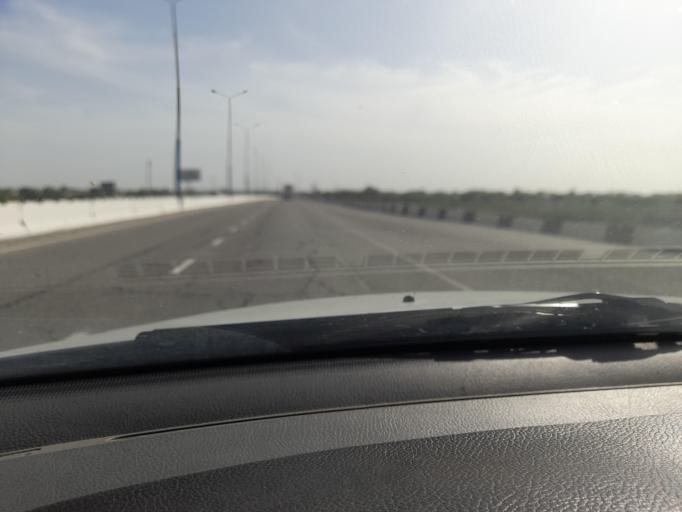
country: UZ
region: Samarqand
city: Kattaqo'rg'on
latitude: 39.9295
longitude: 66.3618
